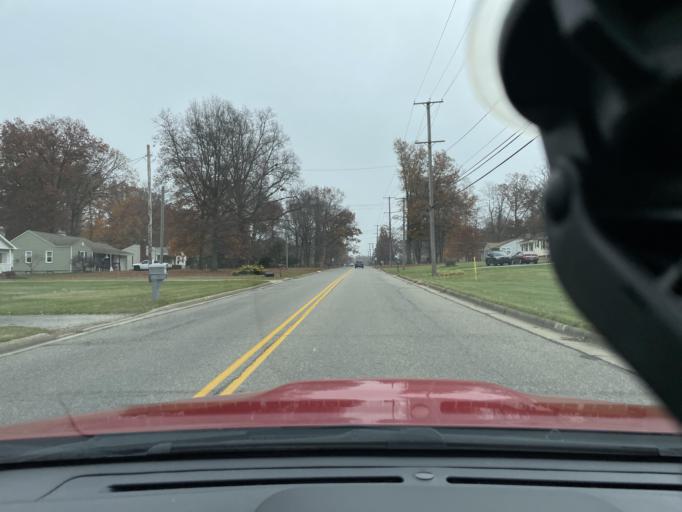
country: US
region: Ohio
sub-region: Mahoning County
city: Austintown
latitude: 41.1058
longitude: -80.7520
